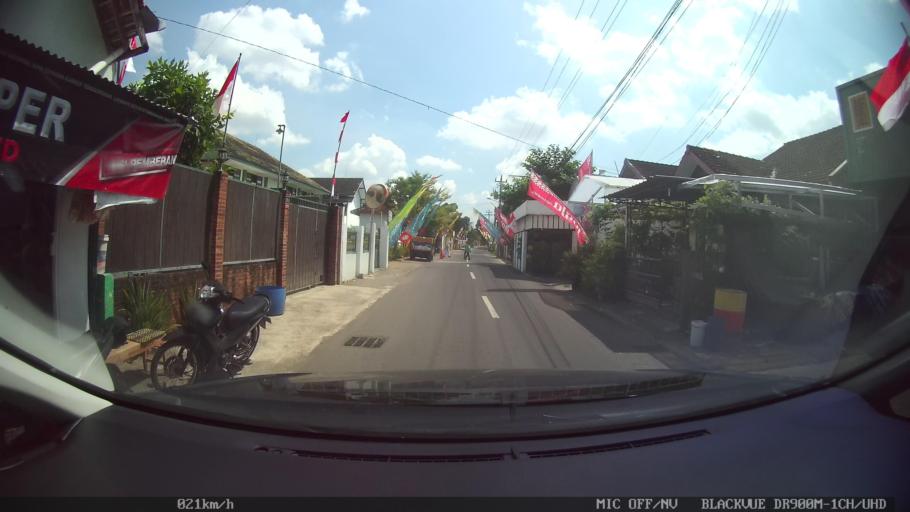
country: ID
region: Daerah Istimewa Yogyakarta
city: Yogyakarta
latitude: -7.8287
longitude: 110.3877
